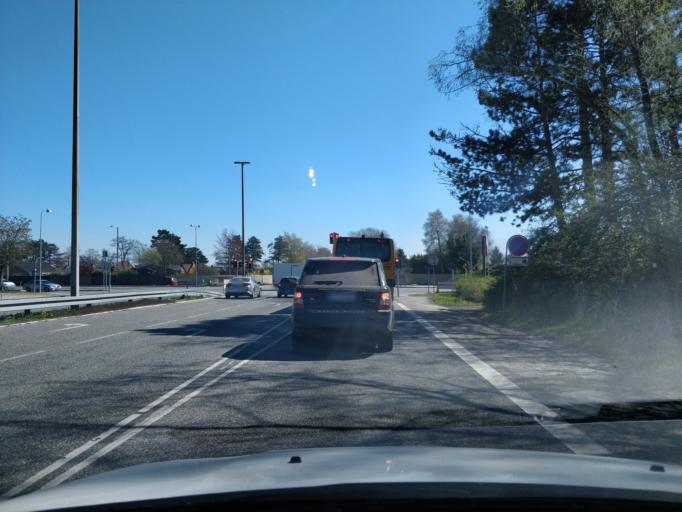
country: DK
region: Capital Region
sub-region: Ishoj Kommune
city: Ishoj
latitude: 55.6128
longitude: 12.3646
